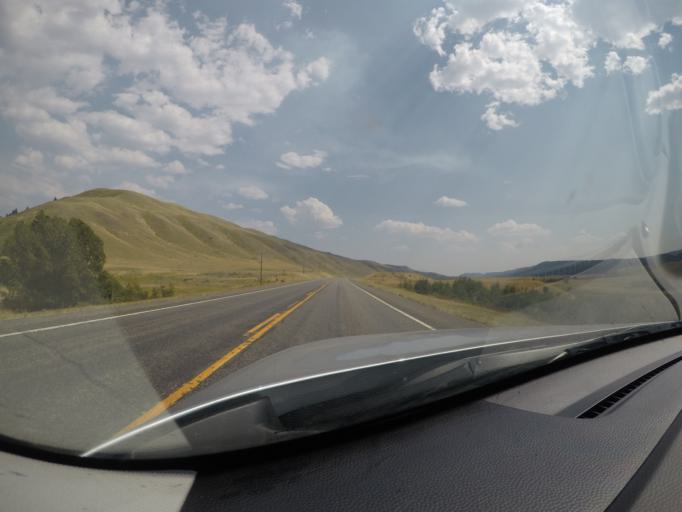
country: US
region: Montana
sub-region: Gallatin County
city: Big Sky
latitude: 44.9601
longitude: -111.6260
